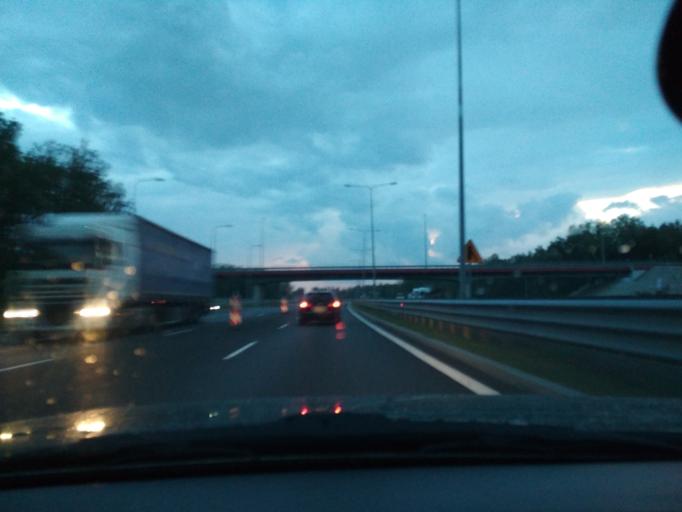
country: PL
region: Silesian Voivodeship
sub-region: Powiat gliwicki
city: Przyszowice
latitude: 50.2855
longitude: 18.7525
